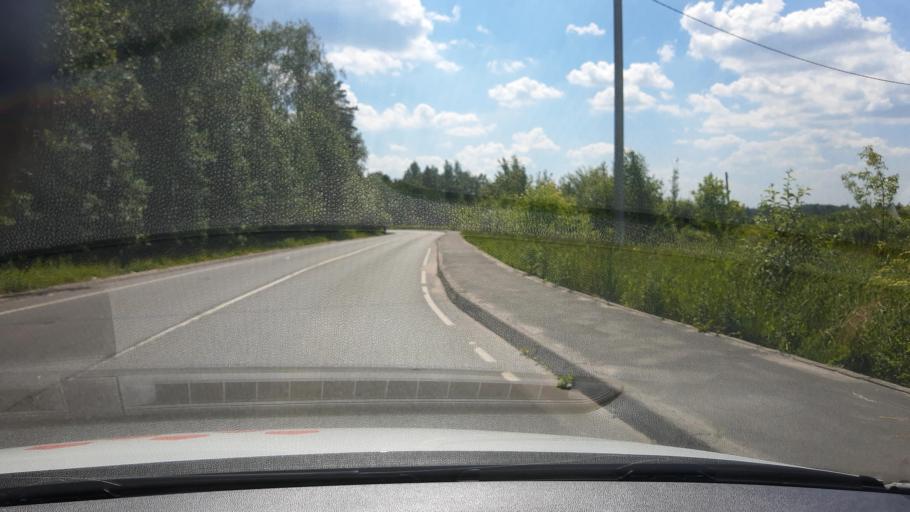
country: RU
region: Moskovskaya
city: Rakhmanovo
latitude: 55.7469
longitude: 38.5386
